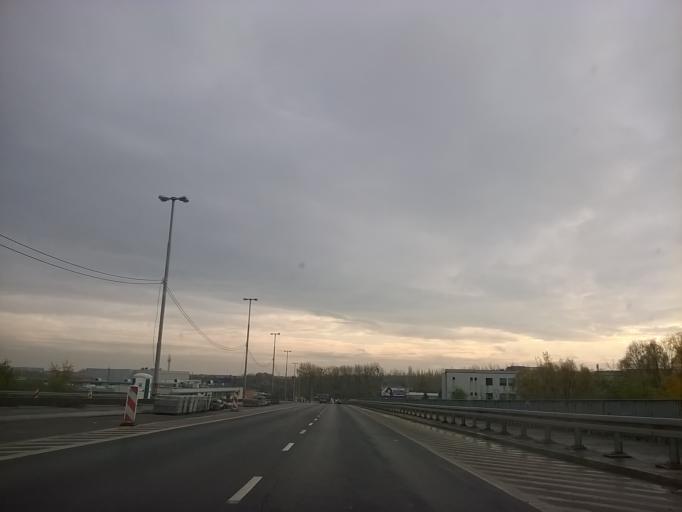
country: PL
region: Pomeranian Voivodeship
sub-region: Powiat gdanski
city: Kowale
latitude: 54.3550
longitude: 18.5888
